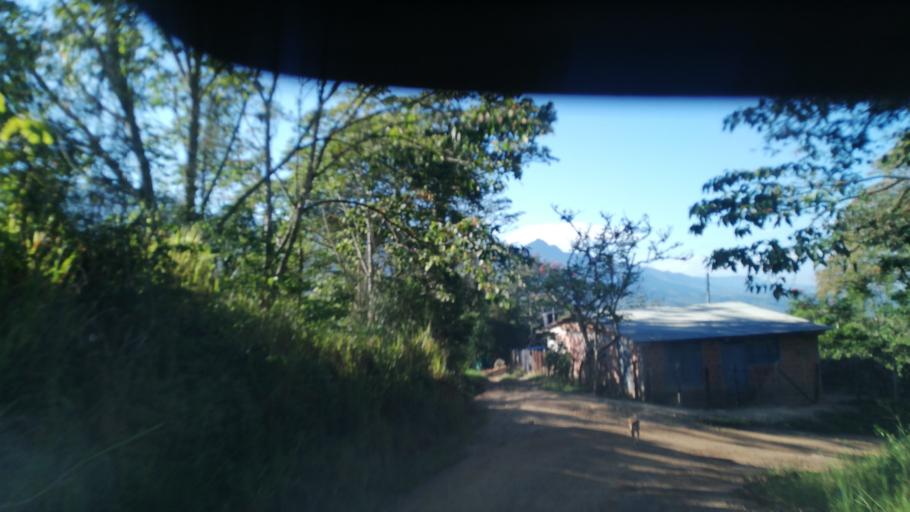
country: CO
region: Cundinamarca
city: Viani
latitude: 4.8386
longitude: -74.6228
